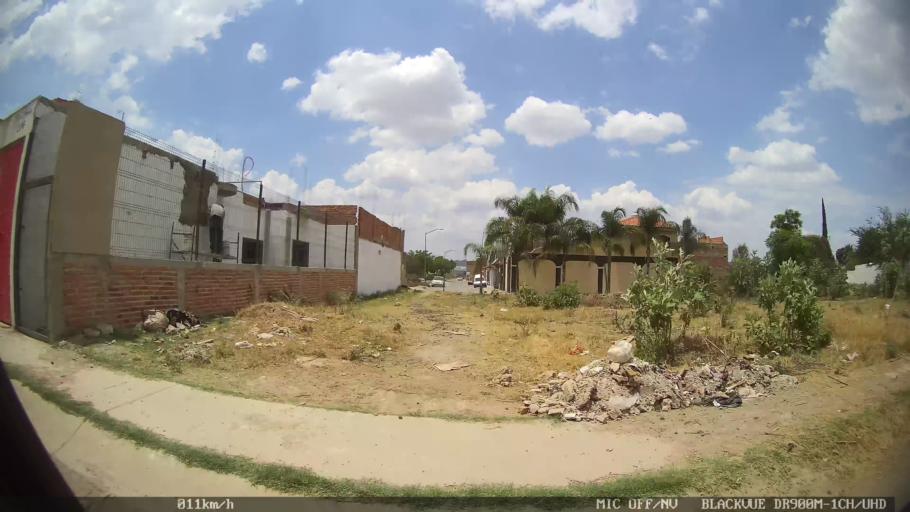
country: MX
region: Jalisco
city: Coyula
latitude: 20.6657
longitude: -103.2266
